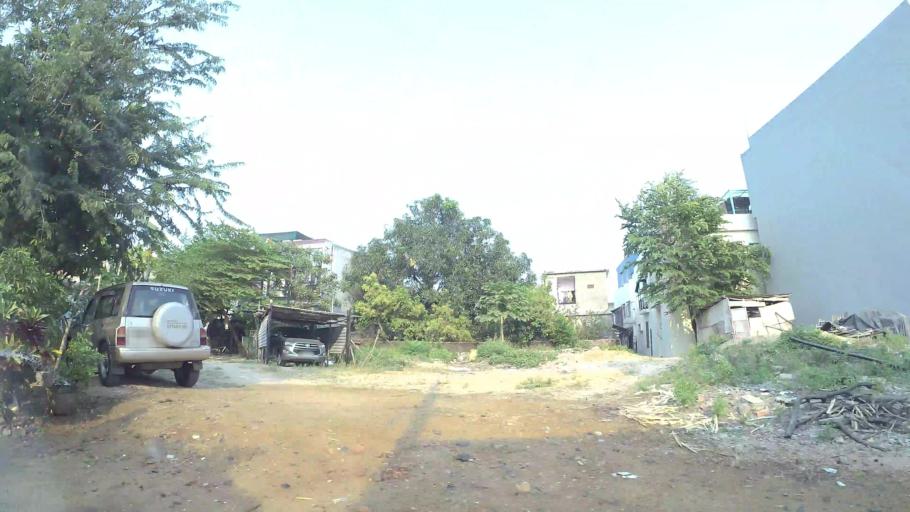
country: VN
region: Da Nang
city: Cam Le
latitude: 16.0193
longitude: 108.2057
